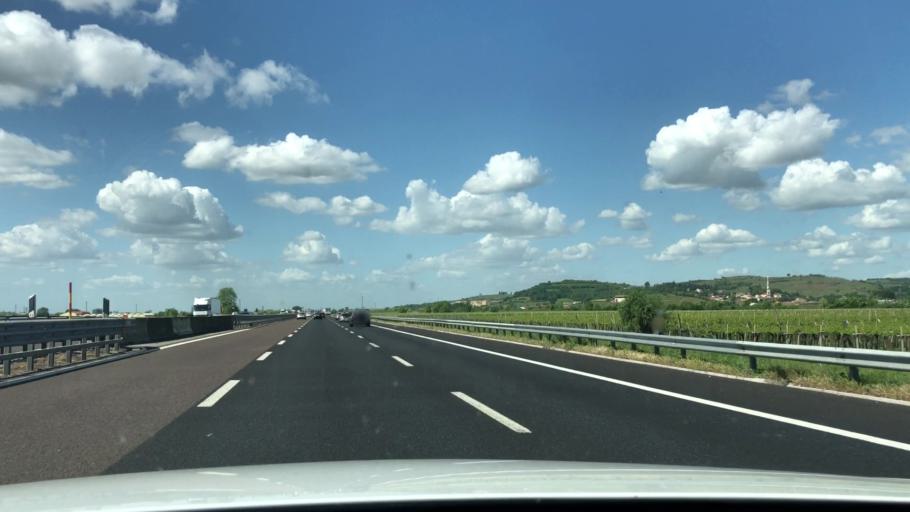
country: IT
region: Veneto
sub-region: Provincia di Verona
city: Locara
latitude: 45.4190
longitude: 11.3124
